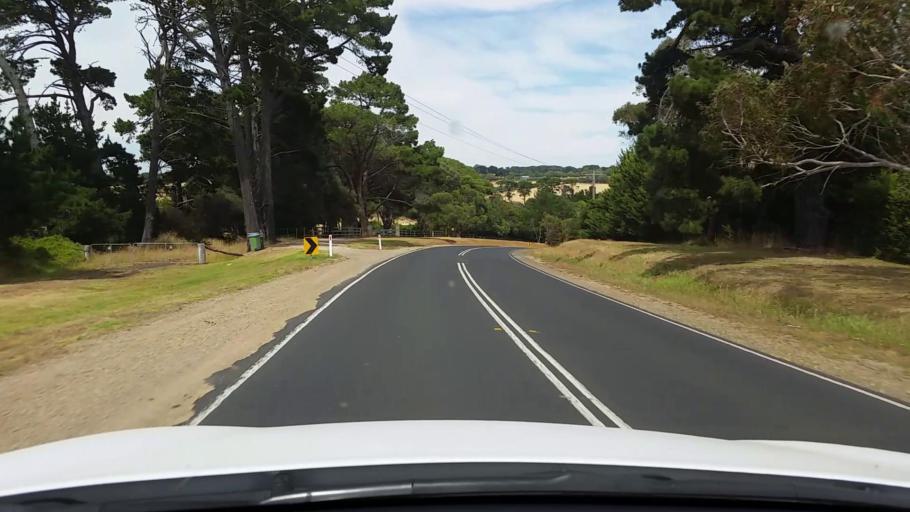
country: AU
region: Victoria
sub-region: Mornington Peninsula
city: Merricks
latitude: -38.4477
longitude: 145.0319
